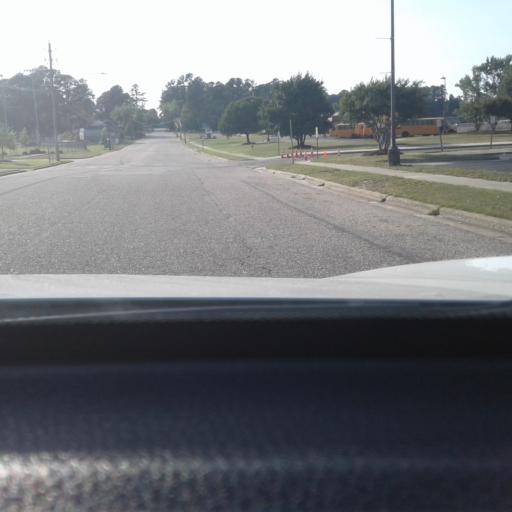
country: US
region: North Carolina
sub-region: Harnett County
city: Dunn
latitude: 35.3139
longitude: -78.6157
